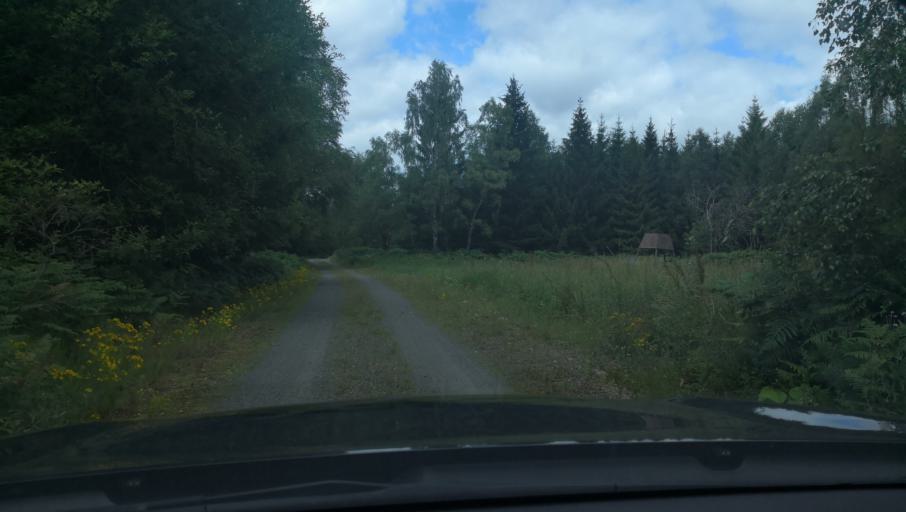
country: SE
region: Skane
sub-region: Simrishamns Kommun
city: Kivik
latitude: 55.6117
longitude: 14.1069
